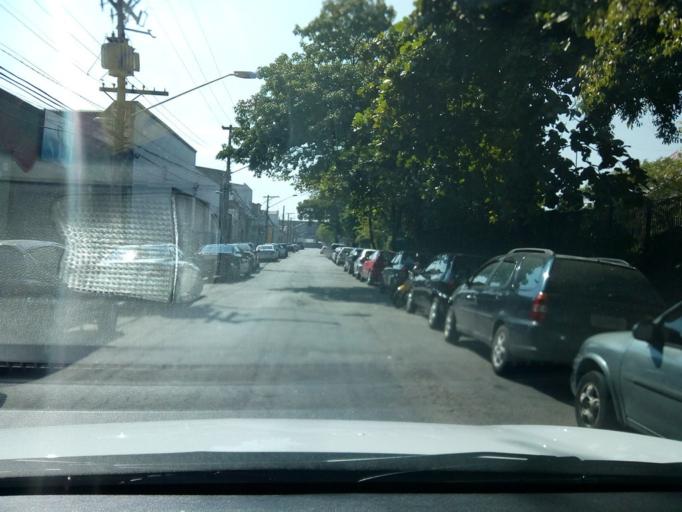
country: BR
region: Sao Paulo
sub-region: Sao Paulo
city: Sao Paulo
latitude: -23.5481
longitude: -46.6187
